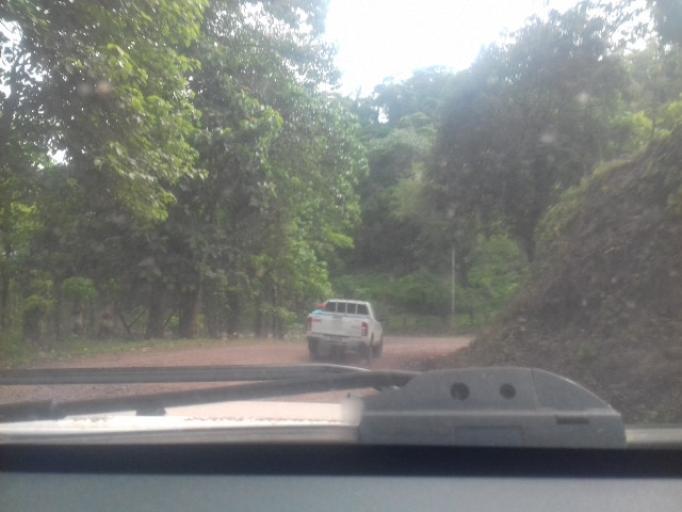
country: NI
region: Atlantico Norte (RAAN)
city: Waslala
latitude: 13.4275
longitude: -85.3127
